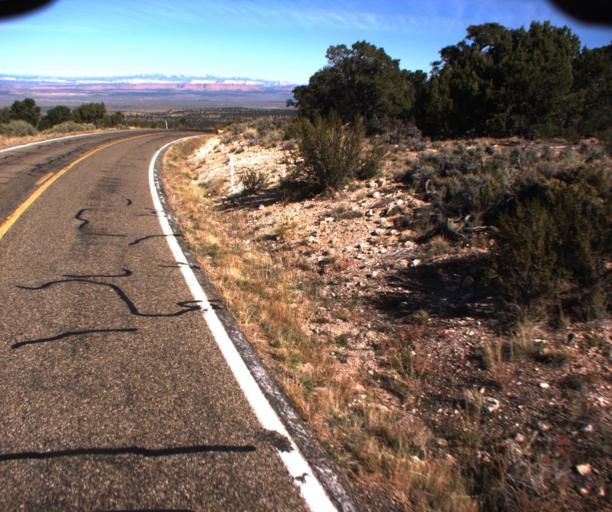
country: US
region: Arizona
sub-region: Coconino County
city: Fredonia
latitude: 36.8382
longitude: -112.2556
